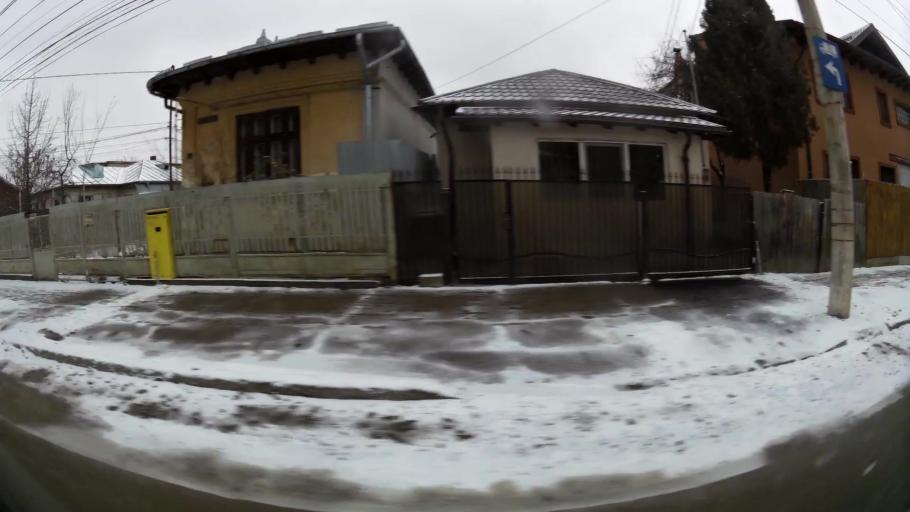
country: RO
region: Prahova
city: Ploiesti
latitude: 44.9301
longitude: 26.0398
